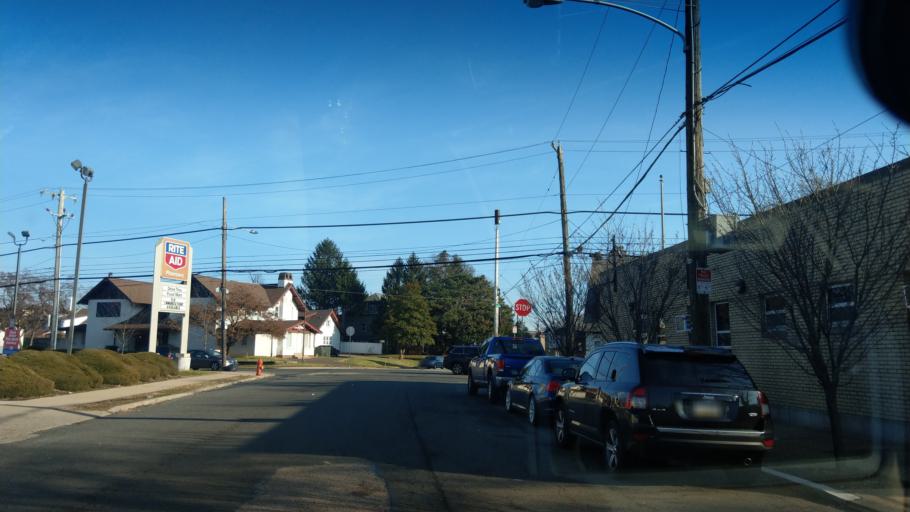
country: US
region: Pennsylvania
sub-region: Montgomery County
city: Rockledge
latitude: 40.0317
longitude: -75.1178
